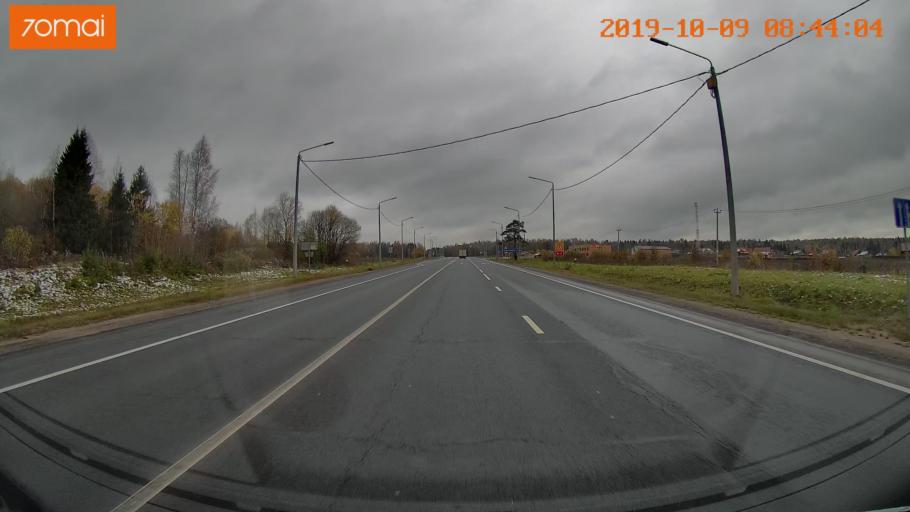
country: RU
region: Vologda
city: Gryazovets
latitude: 59.0314
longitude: 40.1108
